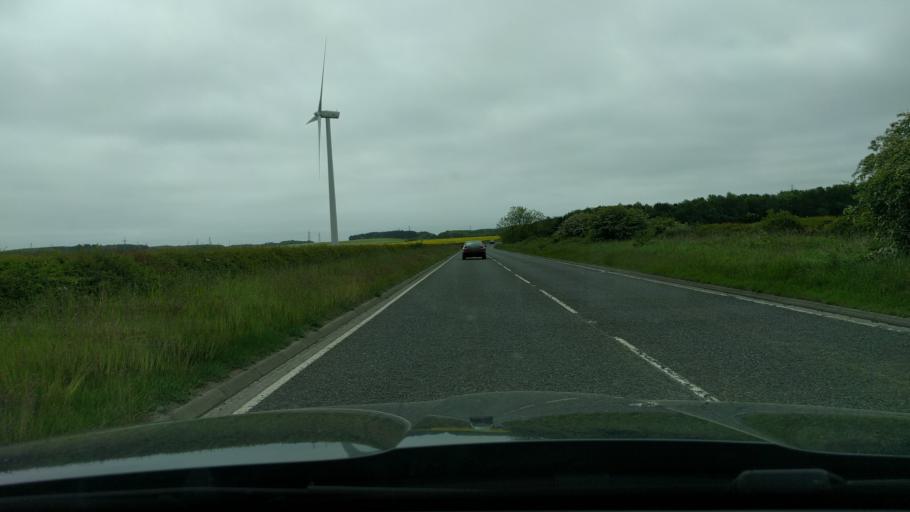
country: GB
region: England
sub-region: Northumberland
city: Cresswell
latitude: 55.2033
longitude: -1.5622
